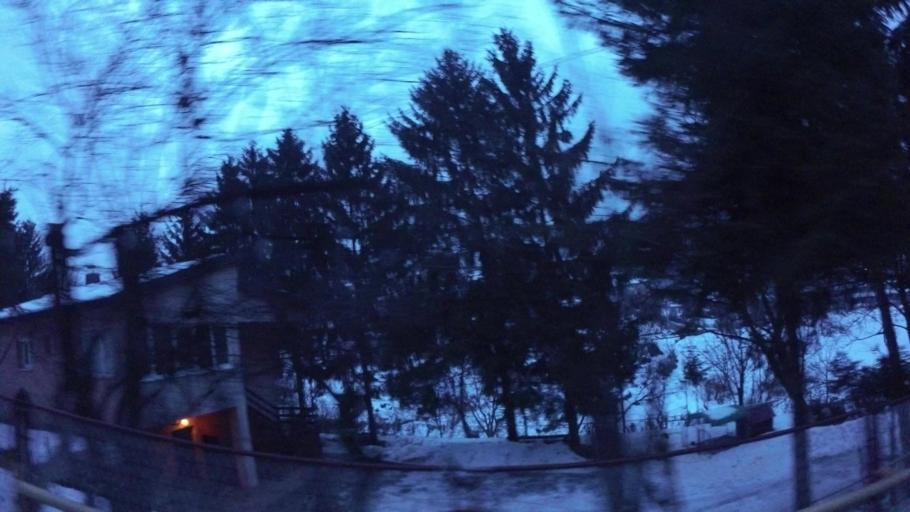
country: BA
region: Federation of Bosnia and Herzegovina
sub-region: Kanton Sarajevo
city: Sarajevo
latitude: 43.8540
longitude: 18.3380
